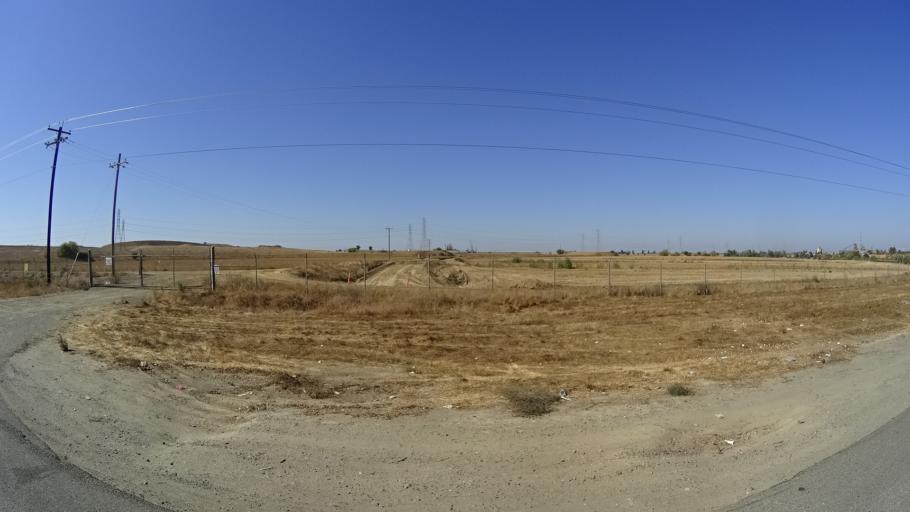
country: US
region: California
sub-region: Sacramento County
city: Rosemont
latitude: 38.5327
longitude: -121.3705
